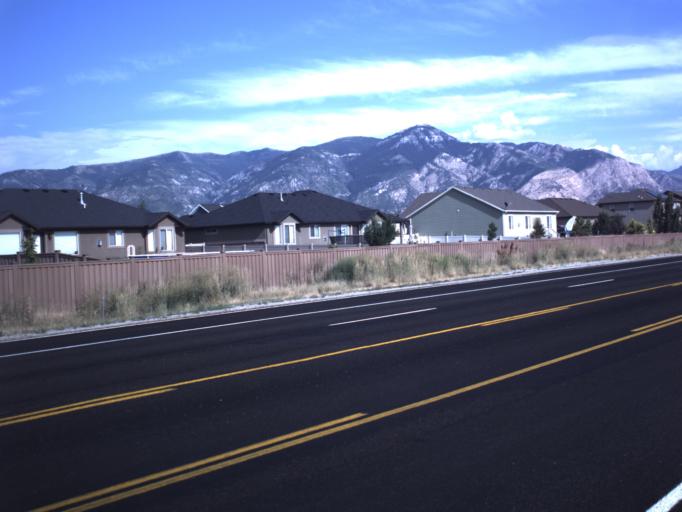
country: US
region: Utah
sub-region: Weber County
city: Pleasant View
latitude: 41.3184
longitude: -112.0147
